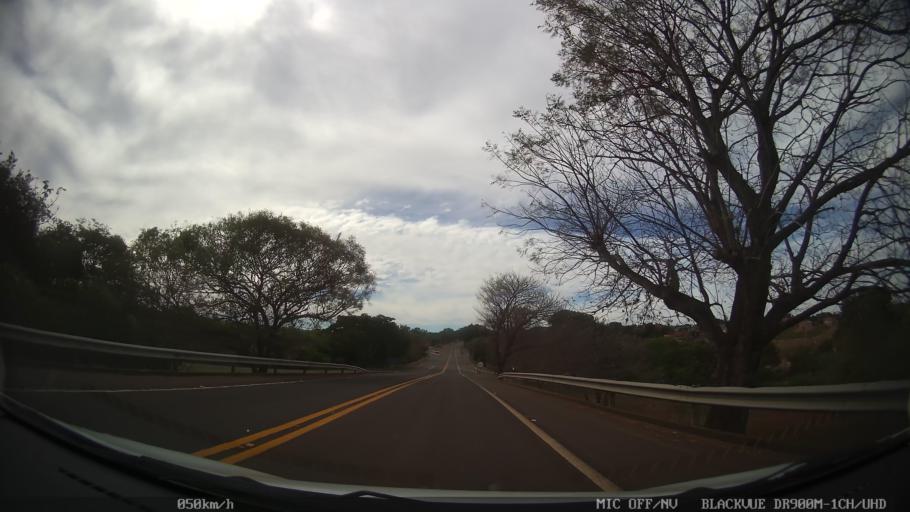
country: BR
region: Sao Paulo
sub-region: Santa Adelia
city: Santa Adelia
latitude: -21.3703
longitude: -48.7484
